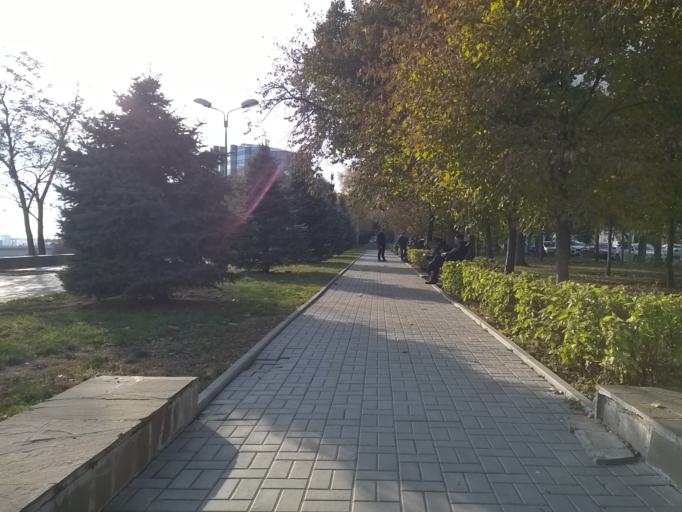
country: RU
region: Rostov
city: Rostov-na-Donu
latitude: 47.2183
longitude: 39.7260
